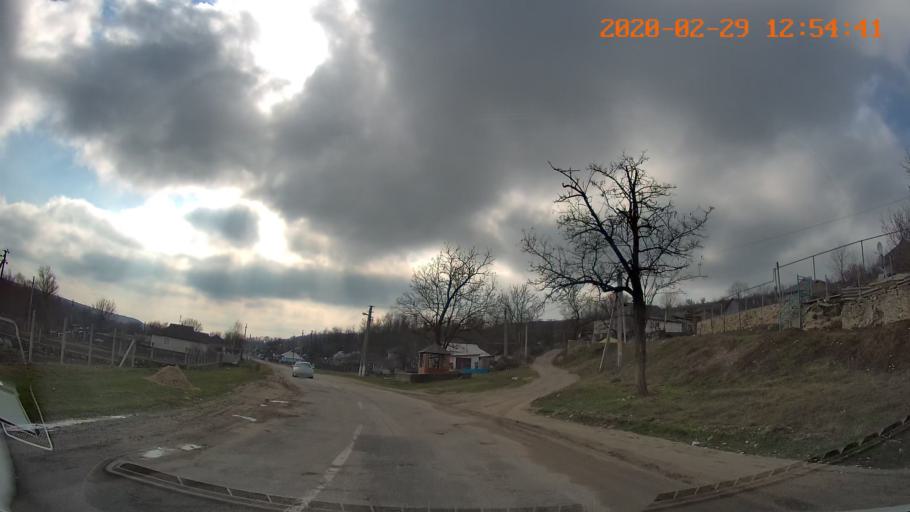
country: MD
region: Telenesti
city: Camenca
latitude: 48.1007
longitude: 28.7257
